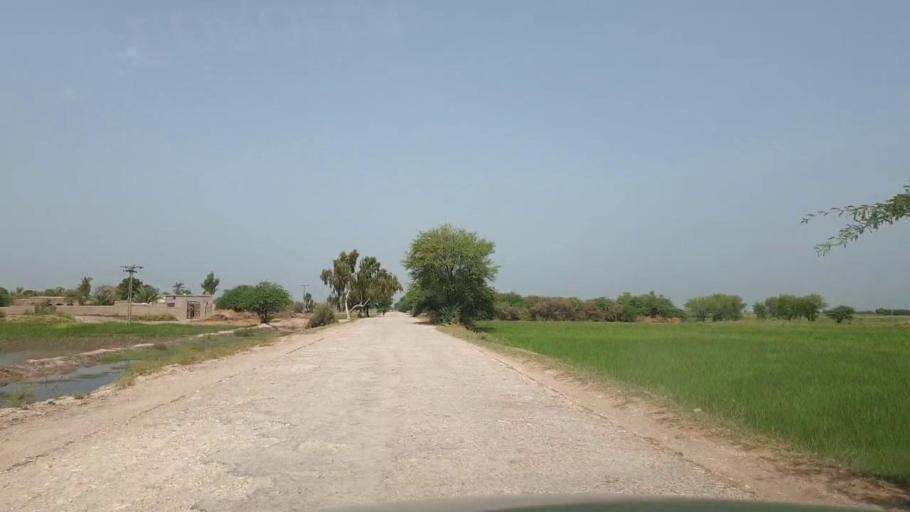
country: PK
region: Sindh
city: Garhi Yasin
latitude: 27.8569
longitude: 68.4168
